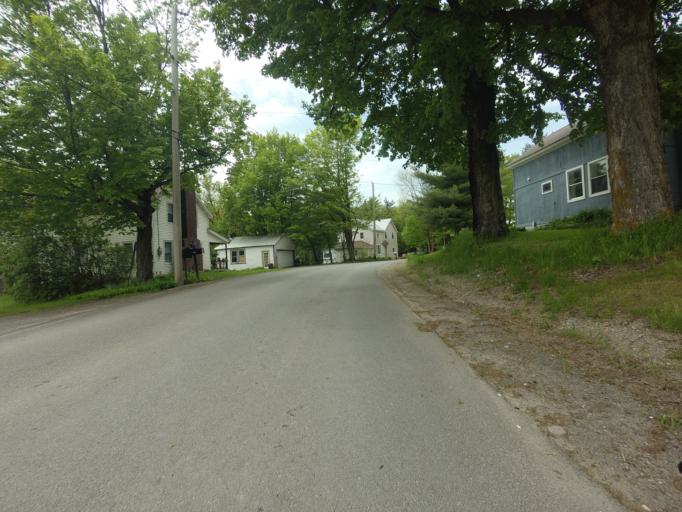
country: US
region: New York
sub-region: St. Lawrence County
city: Hannawa Falls
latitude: 44.5527
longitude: -74.9420
